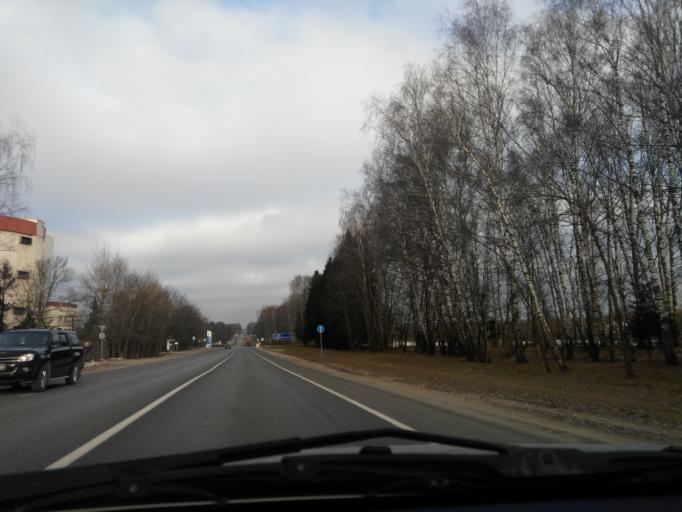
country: RU
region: Moskovskaya
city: Aprelevka
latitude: 55.2839
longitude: 37.1214
